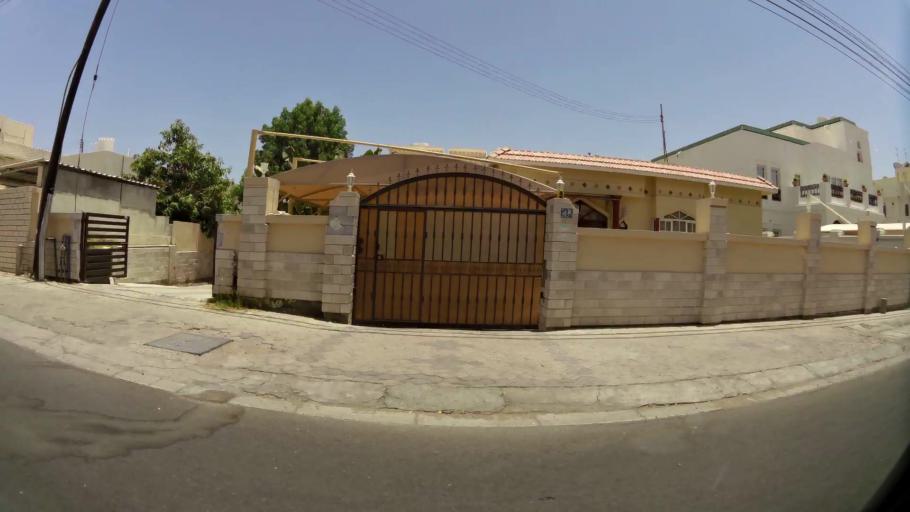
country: OM
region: Muhafazat Masqat
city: Bawshar
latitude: 23.6039
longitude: 58.4621
